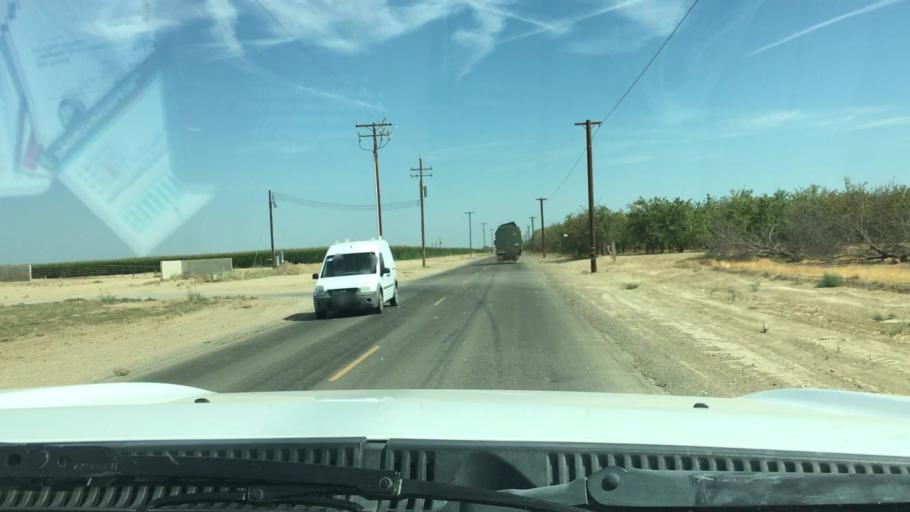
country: US
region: California
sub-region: Kern County
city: Shafter
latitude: 35.4741
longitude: -119.3680
